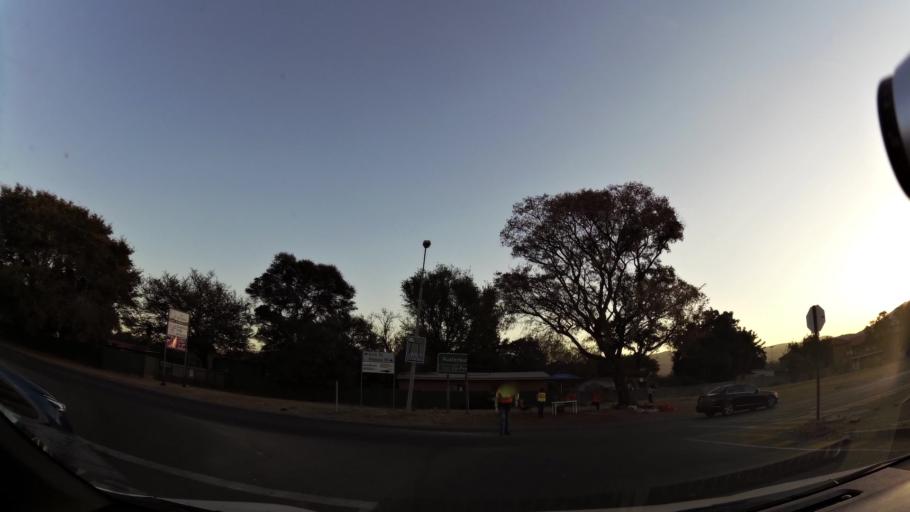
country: ZA
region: North-West
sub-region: Bojanala Platinum District Municipality
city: Rustenburg
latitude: -25.6715
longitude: 27.2255
